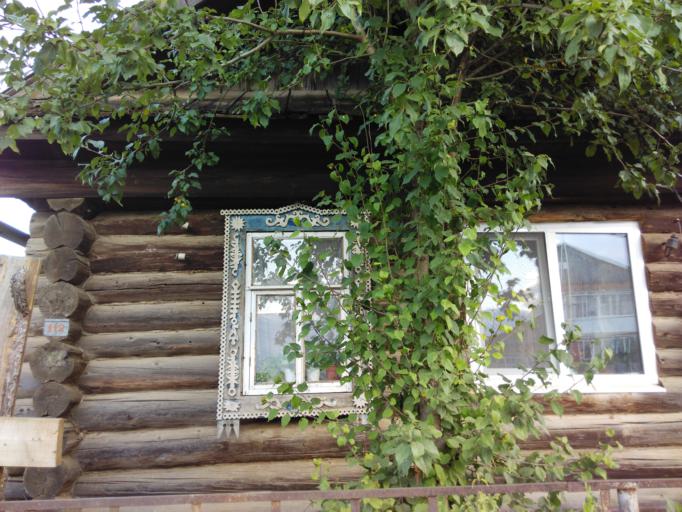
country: RU
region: Perm
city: Foki
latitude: 56.6992
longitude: 54.3553
